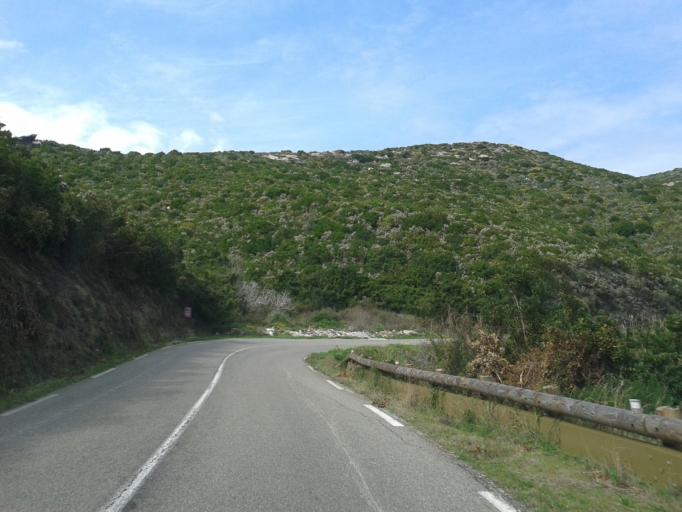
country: FR
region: Corsica
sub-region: Departement de la Haute-Corse
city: Brando
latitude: 42.8469
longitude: 9.4824
